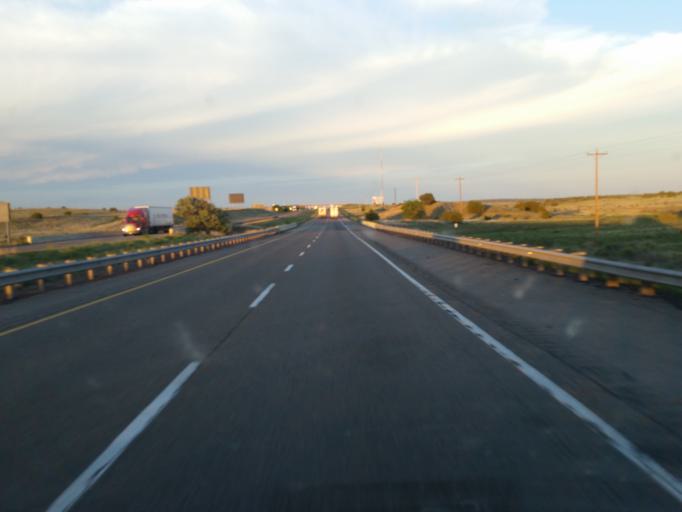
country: US
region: New Mexico
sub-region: San Miguel County
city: Las Vegas
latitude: 34.9920
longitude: -105.3074
